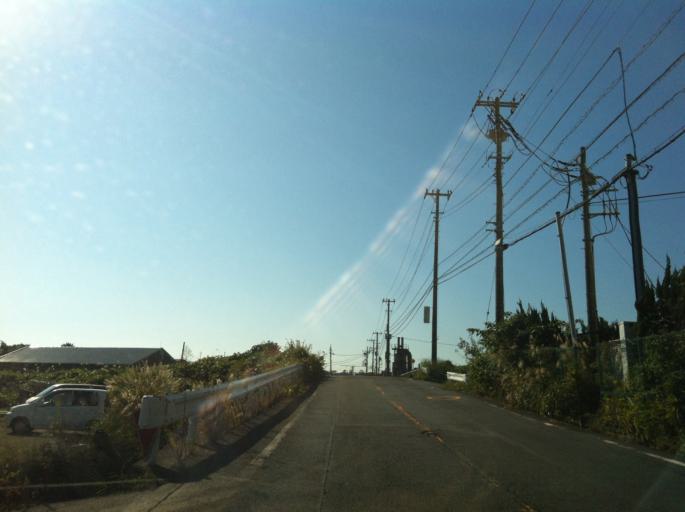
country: JP
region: Shizuoka
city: Fuji
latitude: 35.1367
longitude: 138.7756
